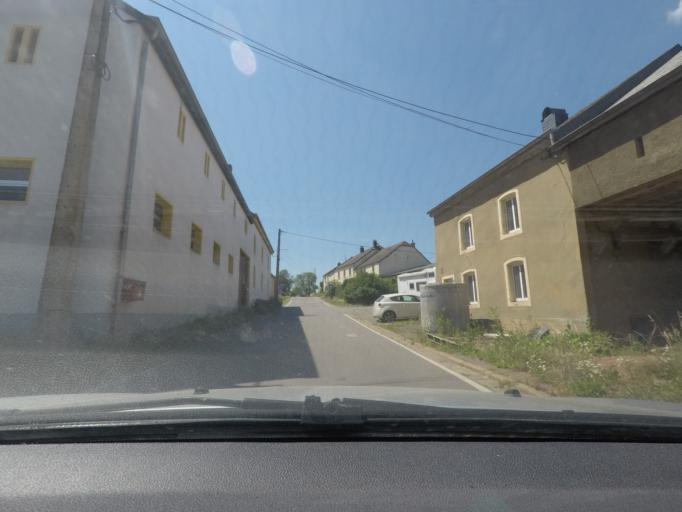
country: BE
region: Wallonia
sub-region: Province du Luxembourg
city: Attert
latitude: 49.7546
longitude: 5.8088
